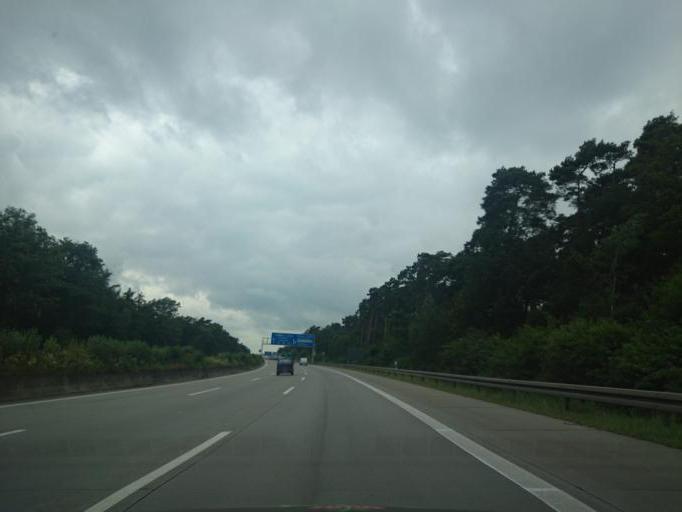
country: DE
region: Brandenburg
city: Schulzendorf
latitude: 52.3199
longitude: 13.5830
